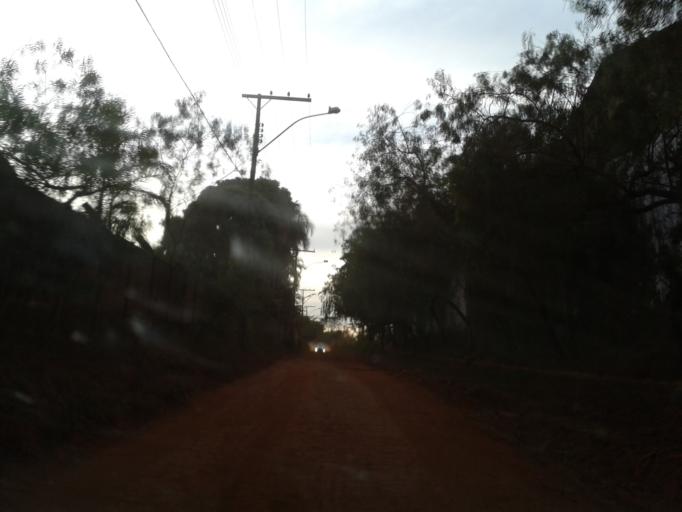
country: BR
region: Goias
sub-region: Goiania
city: Goiania
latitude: -16.6456
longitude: -49.3524
